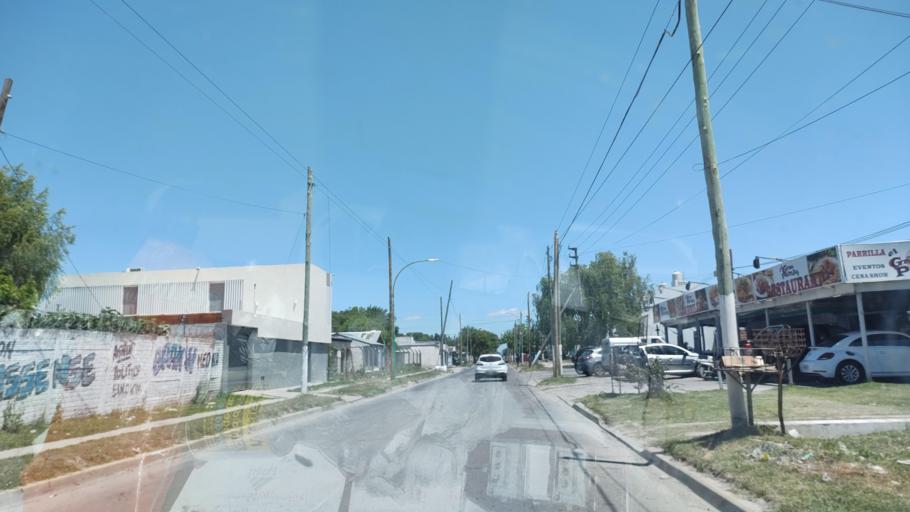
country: AR
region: Buenos Aires
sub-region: Partido de Berisso
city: Berisso
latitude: -34.8814
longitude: -57.8638
